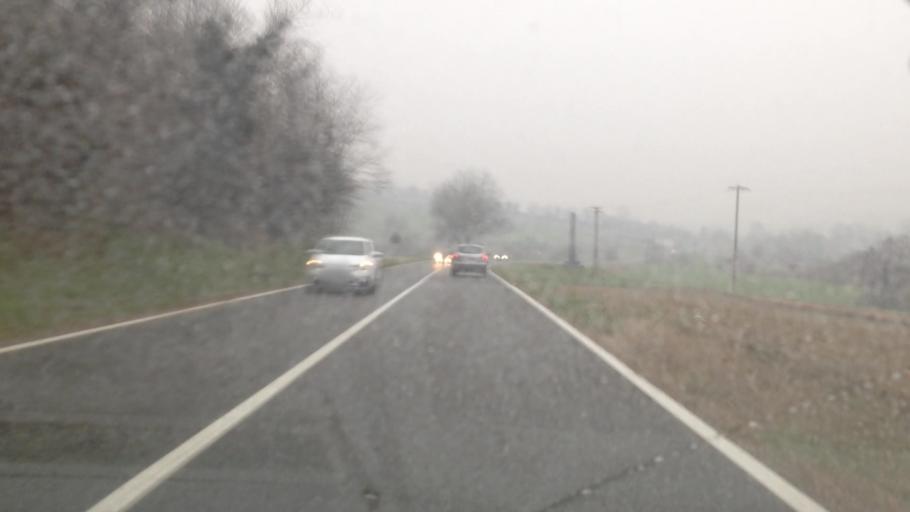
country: IT
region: Piedmont
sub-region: Provincia di Torino
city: Brozolo
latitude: 45.0995
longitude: 8.0814
